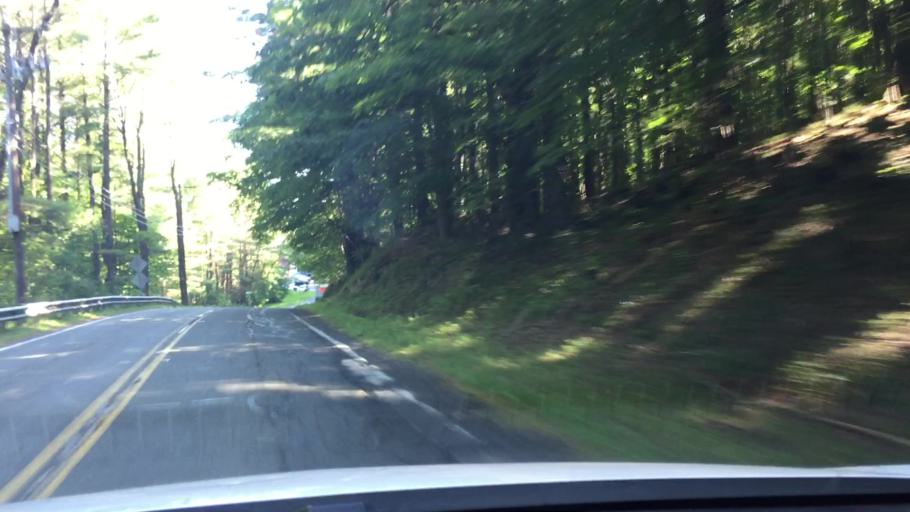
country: US
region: Massachusetts
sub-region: Berkshire County
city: West Stockbridge
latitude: 42.3183
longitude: -73.3687
